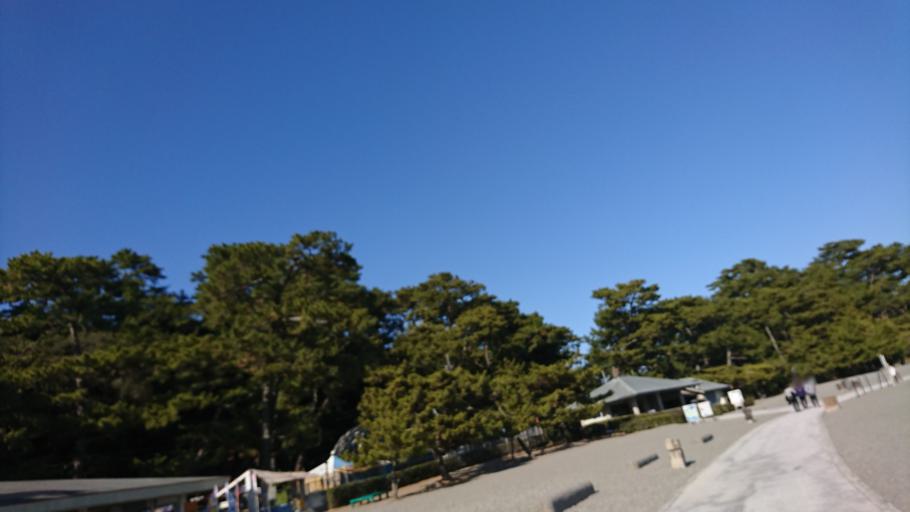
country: JP
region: Kochi
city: Kochi-shi
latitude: 33.4971
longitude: 133.5740
